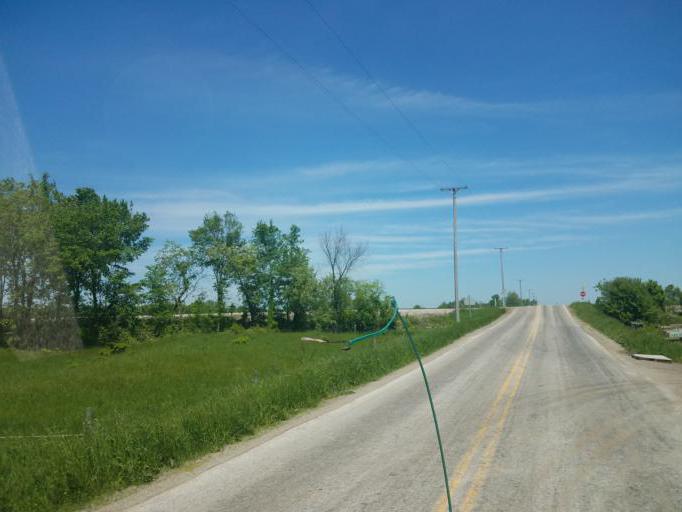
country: US
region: Ohio
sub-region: Ashland County
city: Ashland
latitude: 40.9333
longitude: -82.2433
